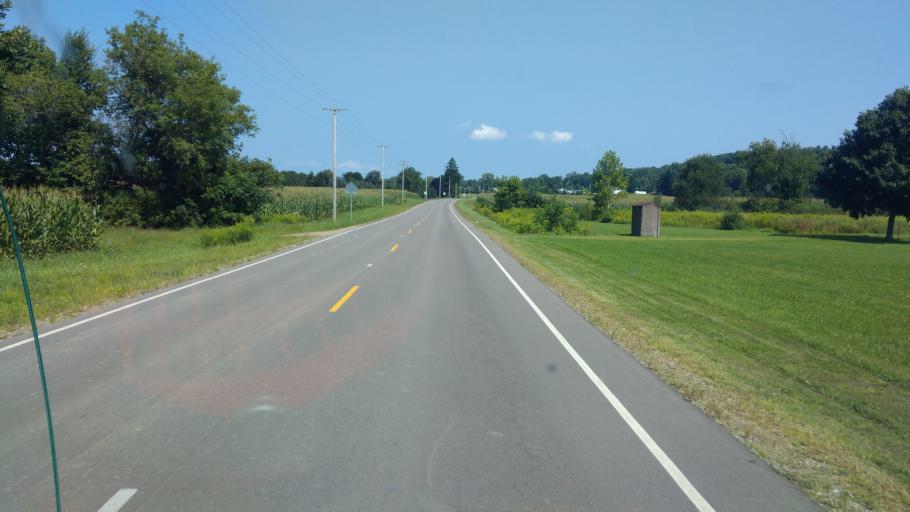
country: US
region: New York
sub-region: Allegany County
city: Belmont
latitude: 42.2420
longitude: -78.0407
